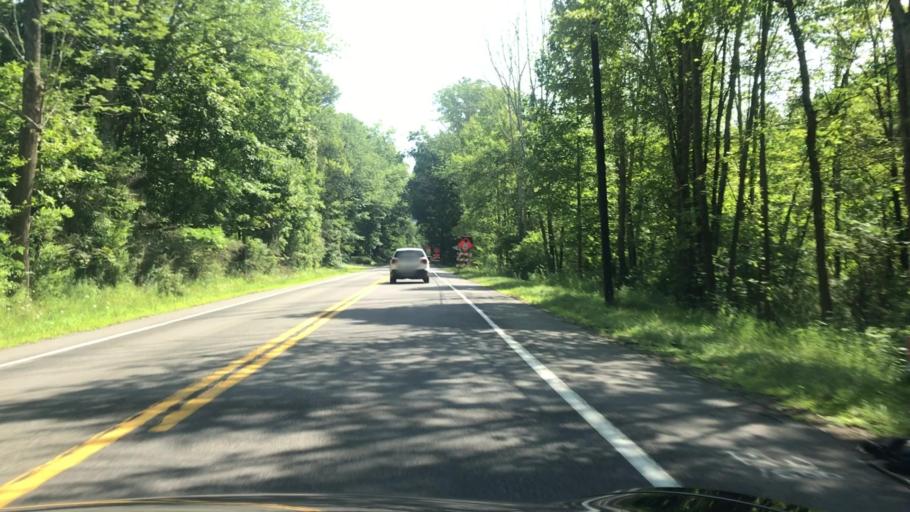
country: US
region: Pennsylvania
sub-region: Lycoming County
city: Garden View
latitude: 41.4208
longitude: -77.0322
